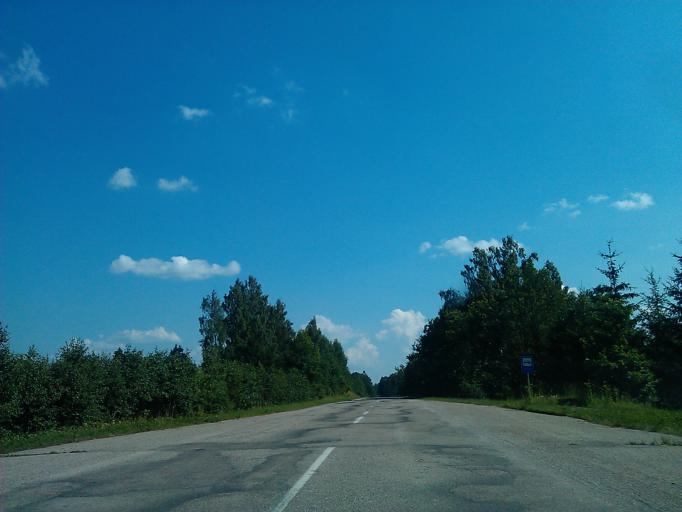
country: LV
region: Aizpute
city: Aizpute
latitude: 56.6471
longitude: 21.6580
